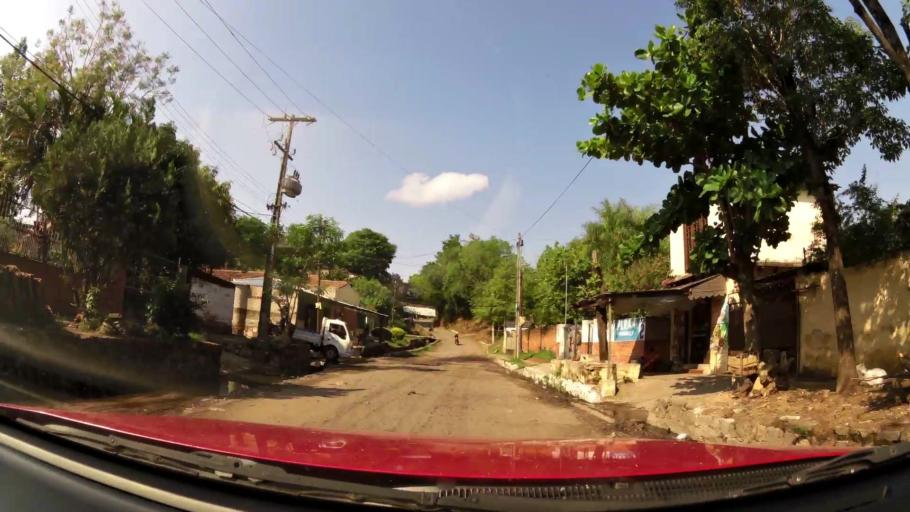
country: PY
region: Asuncion
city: Asuncion
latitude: -25.3209
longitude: -57.6429
